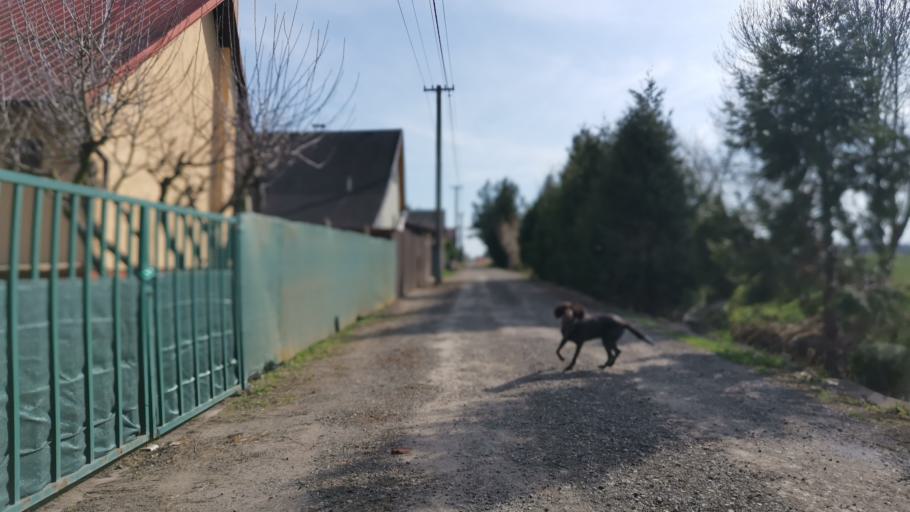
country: CZ
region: South Moravian
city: Tvrdonice
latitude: 48.7301
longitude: 17.0243
